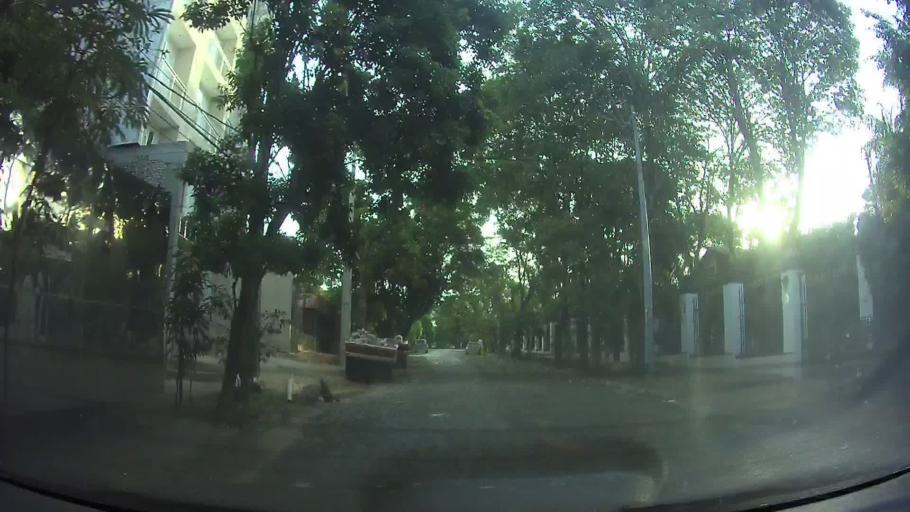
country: PY
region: Asuncion
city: Asuncion
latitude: -25.2758
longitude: -57.5707
